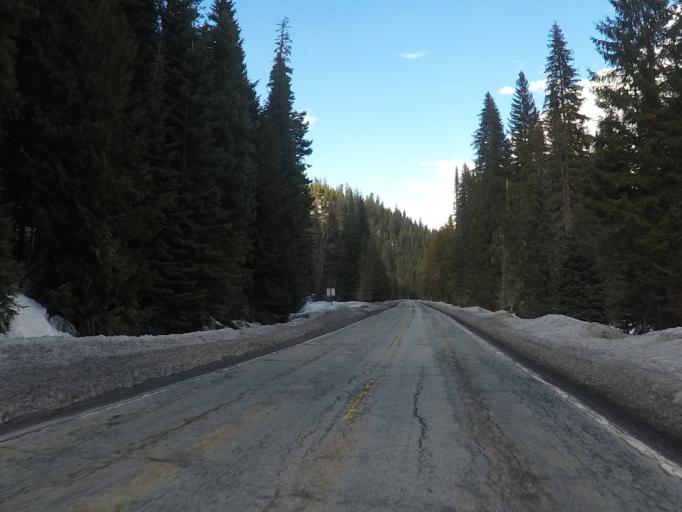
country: US
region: Montana
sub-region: Ravalli County
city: Stevensville
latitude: 46.5670
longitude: -114.6408
